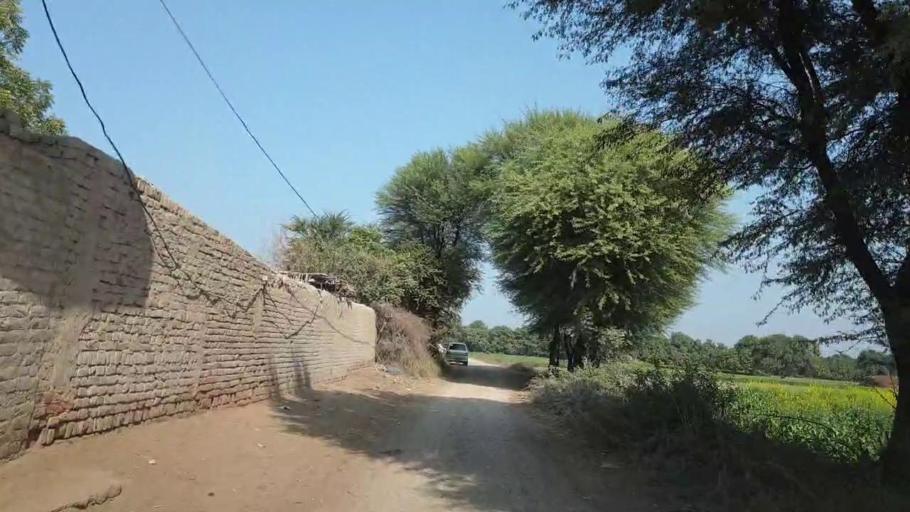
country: PK
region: Sindh
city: Bhit Shah
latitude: 25.7484
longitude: 68.4791
